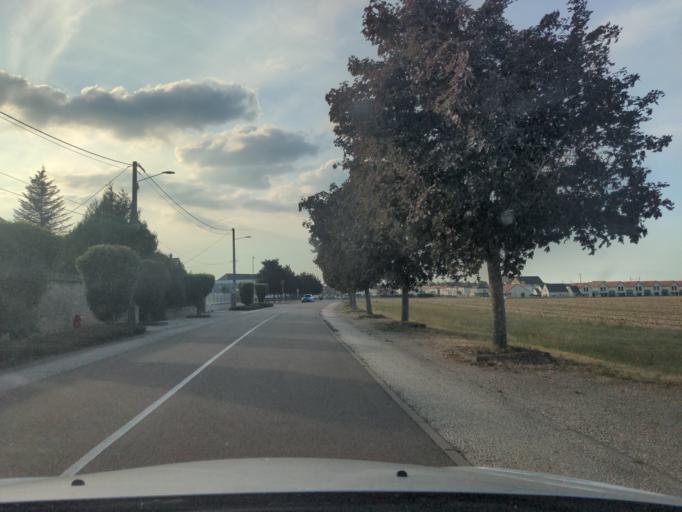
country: FR
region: Bourgogne
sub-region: Departement de la Cote-d'Or
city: Neuilly-les-Dijon
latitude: 47.2754
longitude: 5.1201
